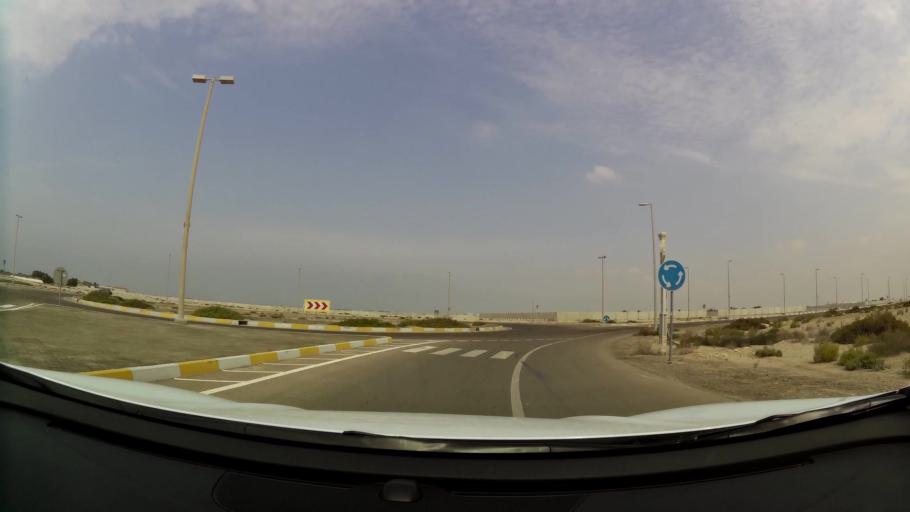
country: AE
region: Abu Dhabi
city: Abu Dhabi
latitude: 24.6508
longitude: 54.6780
